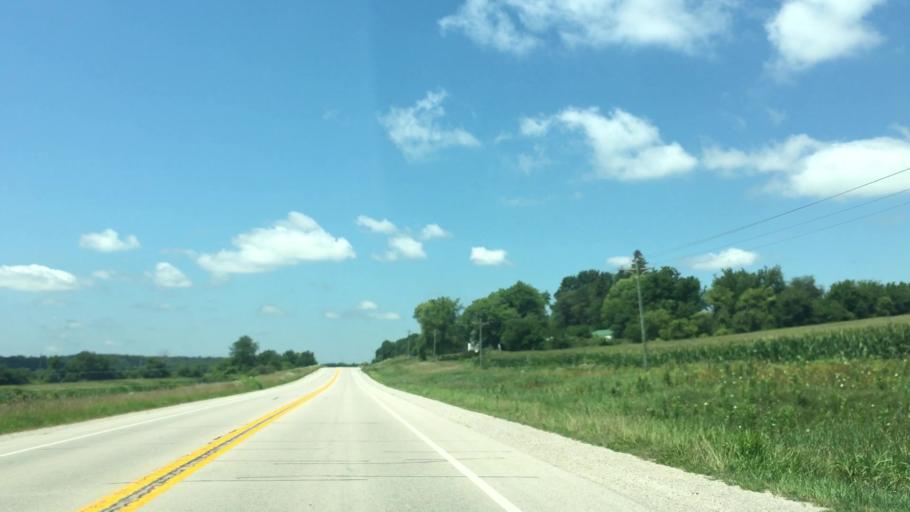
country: US
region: Iowa
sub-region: Johnson County
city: Tiffin
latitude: 41.7150
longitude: -91.7175
